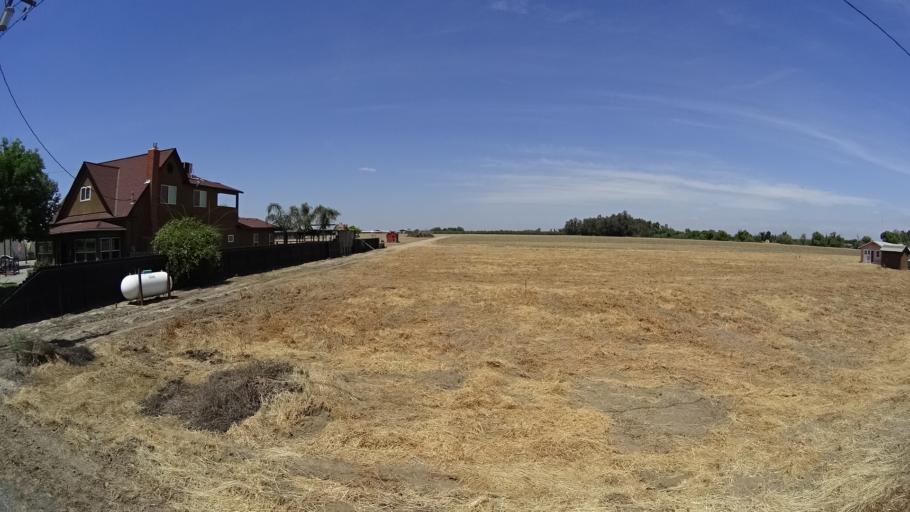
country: US
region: California
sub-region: Kings County
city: Armona
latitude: 36.2839
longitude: -119.6944
